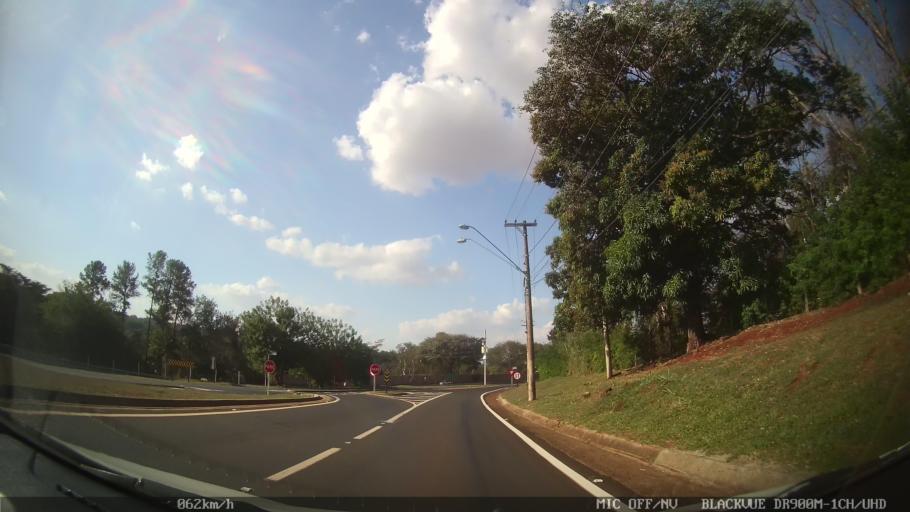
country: BR
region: Sao Paulo
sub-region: Ribeirao Preto
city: Ribeirao Preto
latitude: -21.1769
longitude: -47.8531
